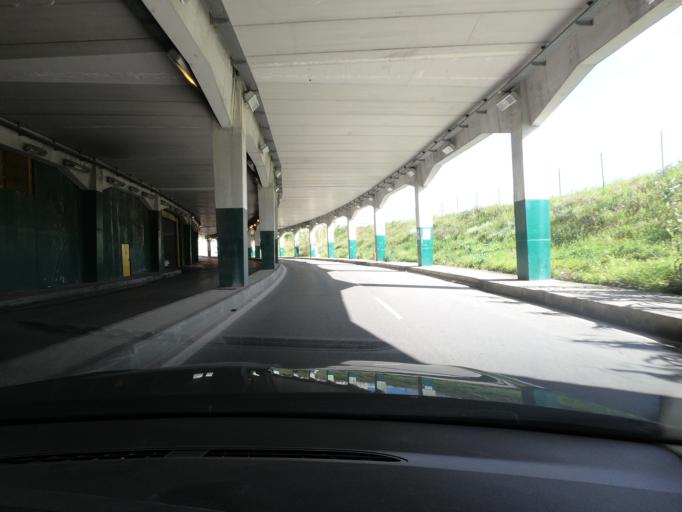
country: PT
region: Lisbon
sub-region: Odivelas
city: Olival do Basto
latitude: 38.7615
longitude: -9.1592
